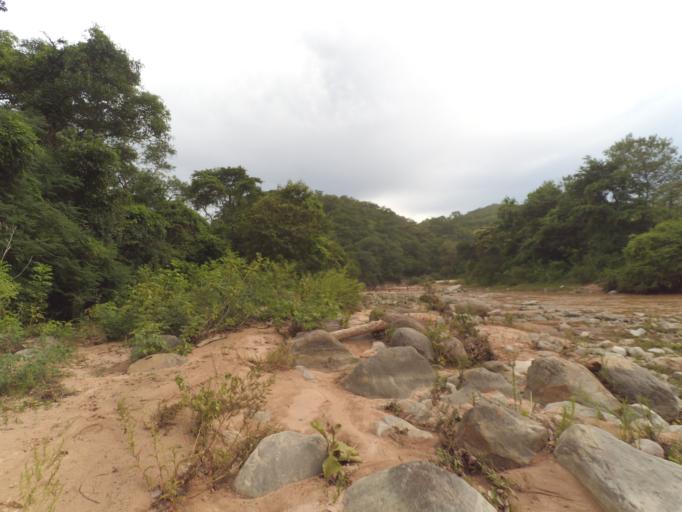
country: BO
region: Chuquisaca
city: Monteagudo
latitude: -19.8022
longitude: -64.0112
